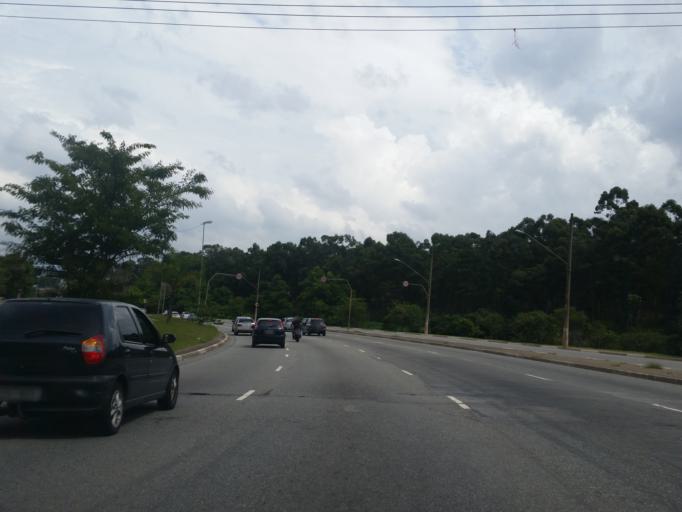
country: BR
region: Sao Paulo
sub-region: Guarulhos
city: Guarulhos
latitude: -23.5006
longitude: -46.4585
